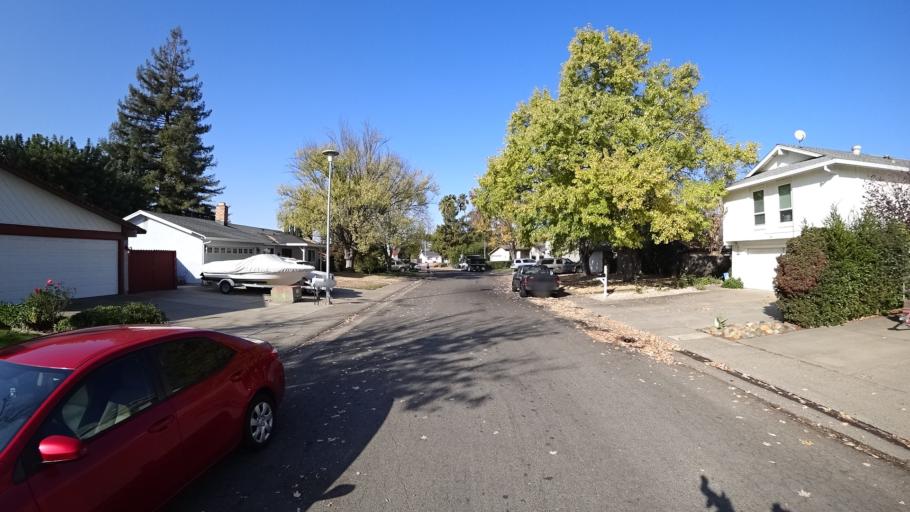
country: US
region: California
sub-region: Sacramento County
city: Orangevale
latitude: 38.6950
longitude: -121.2481
